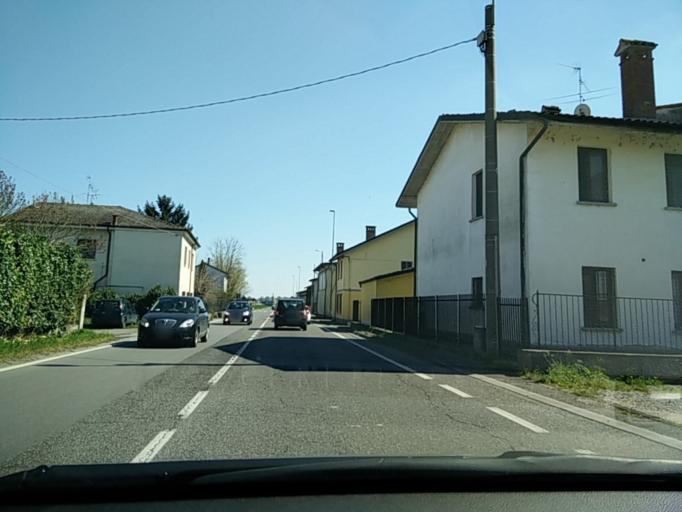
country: IT
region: Lombardy
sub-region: Provincia di Pavia
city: Albaredo Arnaboldi
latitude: 45.1158
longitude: 9.2357
